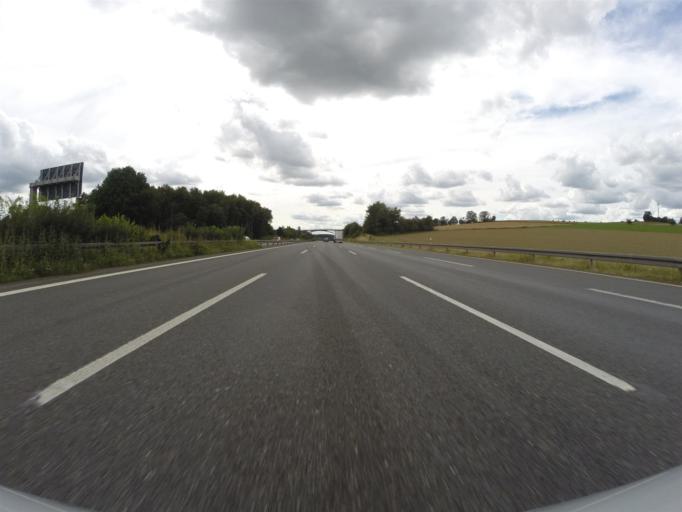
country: DE
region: Bavaria
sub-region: Upper Franconia
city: Marktschorgast
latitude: 50.0815
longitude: 11.6649
